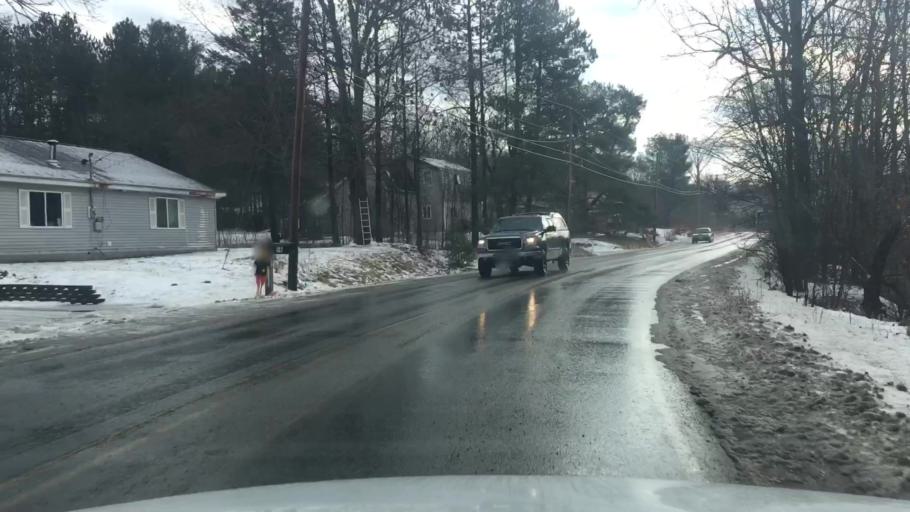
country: US
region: Maine
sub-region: Penobscot County
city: Brewer
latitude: 44.7647
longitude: -68.7773
